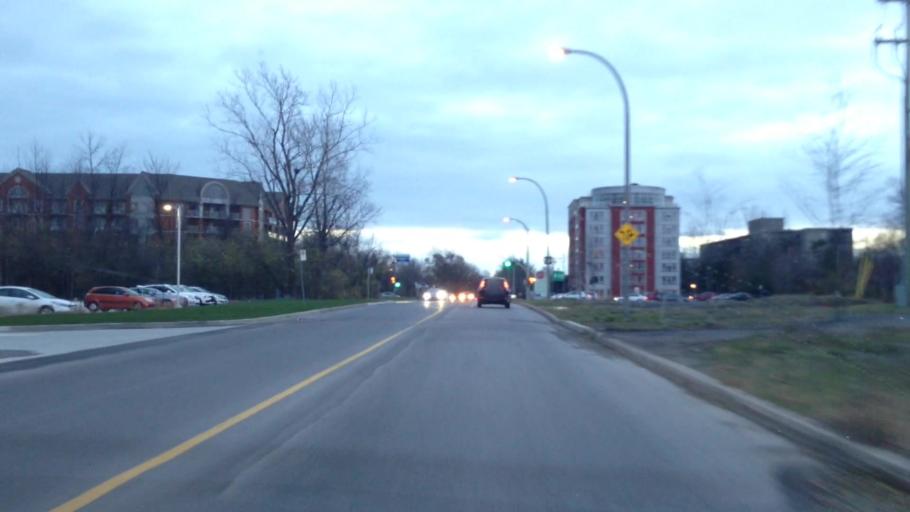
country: CA
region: Quebec
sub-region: Montreal
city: Pointe-Claire
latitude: 45.4540
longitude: -73.8371
